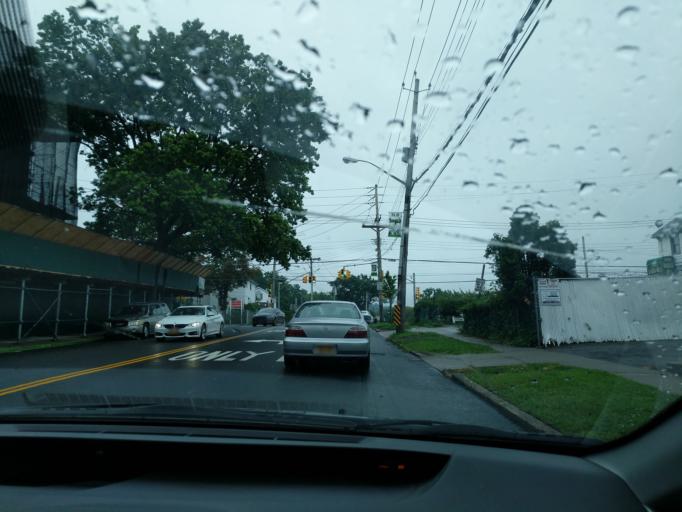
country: US
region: New Jersey
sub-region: Hudson County
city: Bayonne
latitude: 40.6140
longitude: -74.1169
